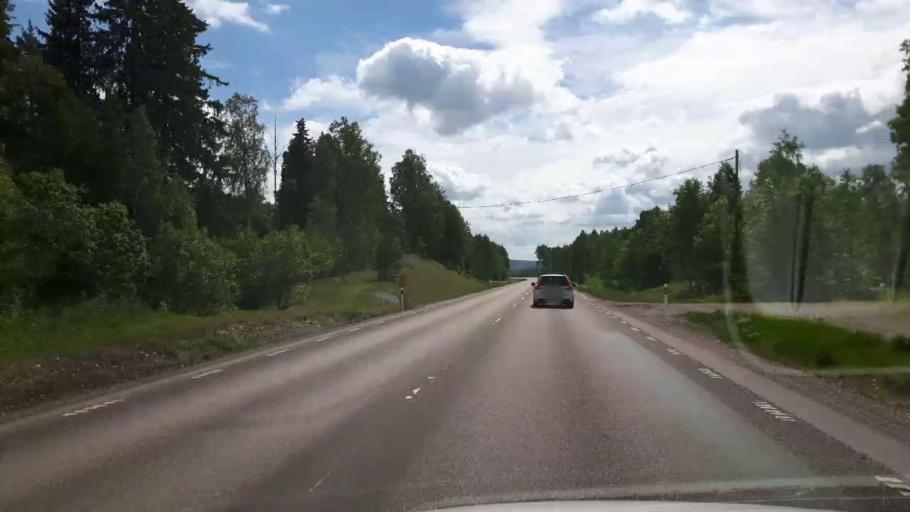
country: SE
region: Dalarna
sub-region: Saters Kommun
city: Saeter
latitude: 60.4467
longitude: 15.8087
